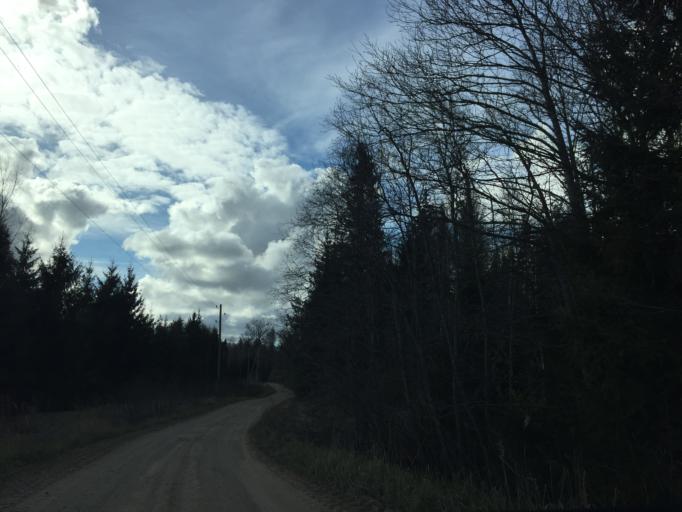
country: LV
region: Burtnieki
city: Matisi
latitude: 57.6141
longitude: 25.0087
